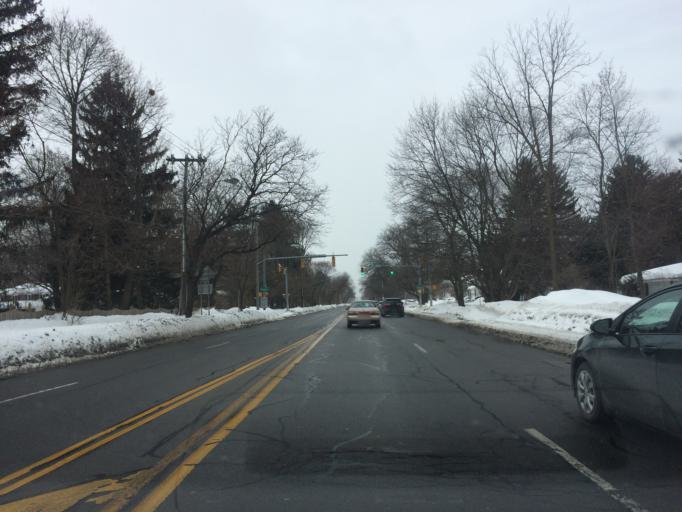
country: US
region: New York
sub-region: Monroe County
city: Brighton
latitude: 43.1264
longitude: -77.5671
